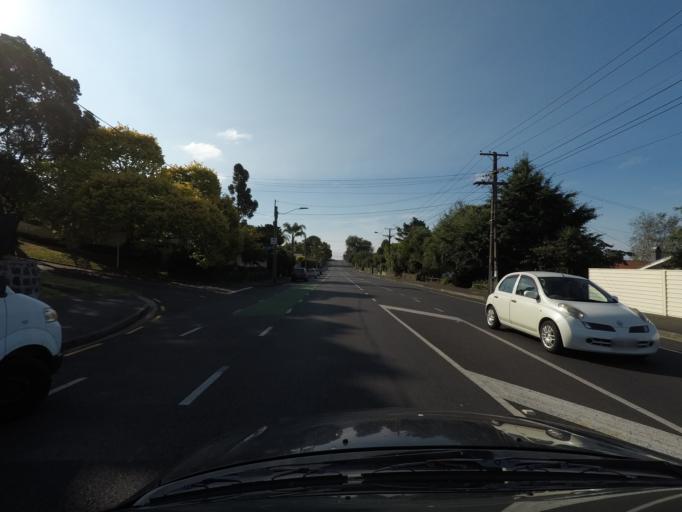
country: NZ
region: Auckland
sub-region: Auckland
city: Auckland
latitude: -36.8887
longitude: 174.7224
